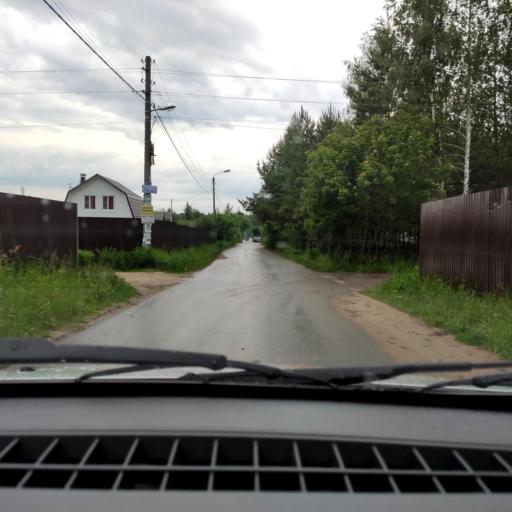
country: RU
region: Voronezj
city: Ramon'
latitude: 51.8588
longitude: 39.2502
